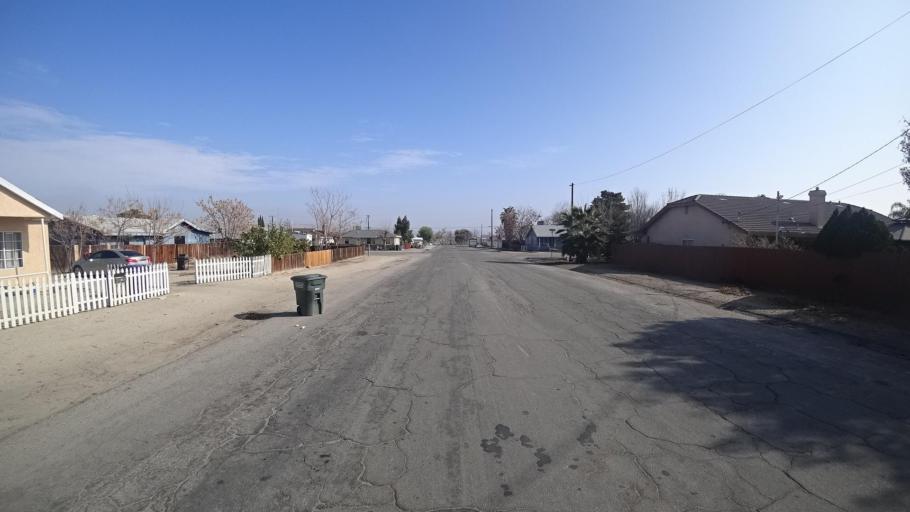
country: US
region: California
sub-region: Kern County
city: Ford City
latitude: 35.1579
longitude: -119.4545
